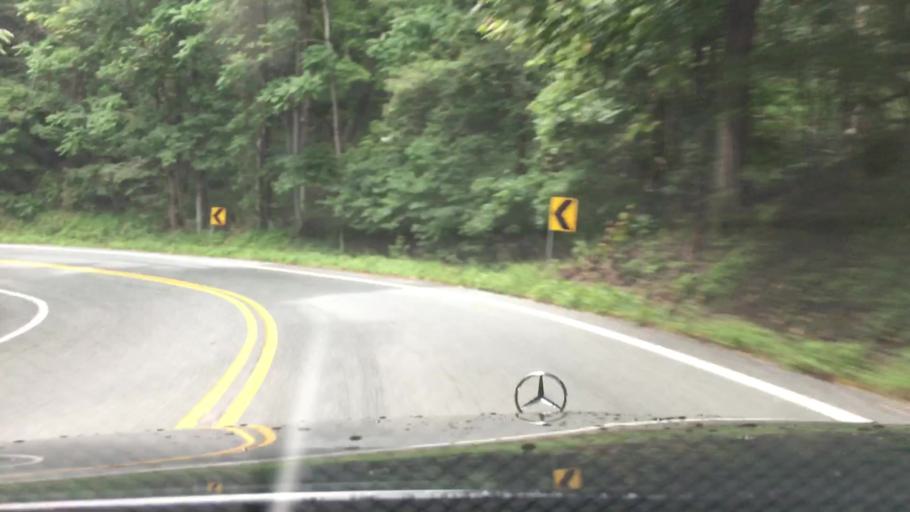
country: US
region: Virginia
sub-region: Nelson County
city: Nellysford
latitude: 37.8513
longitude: -78.9270
